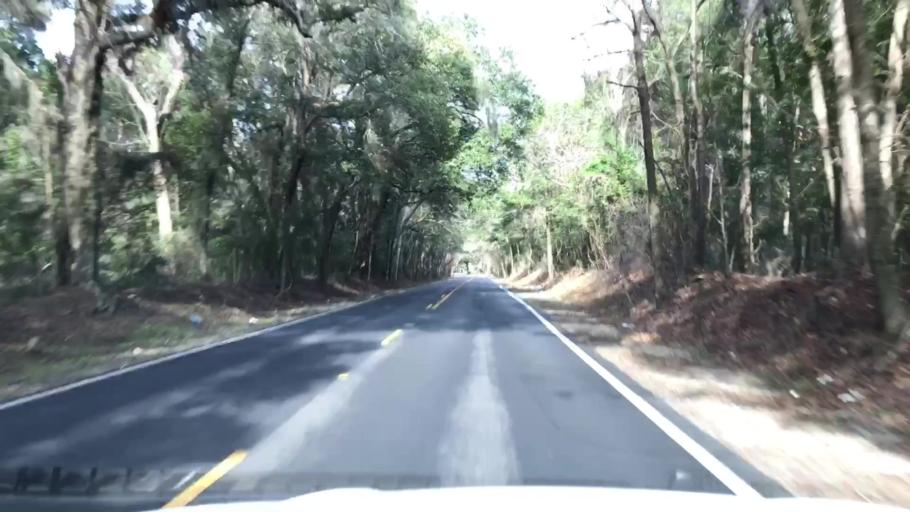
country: US
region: South Carolina
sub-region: Charleston County
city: Folly Beach
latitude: 32.7111
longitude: -80.0180
